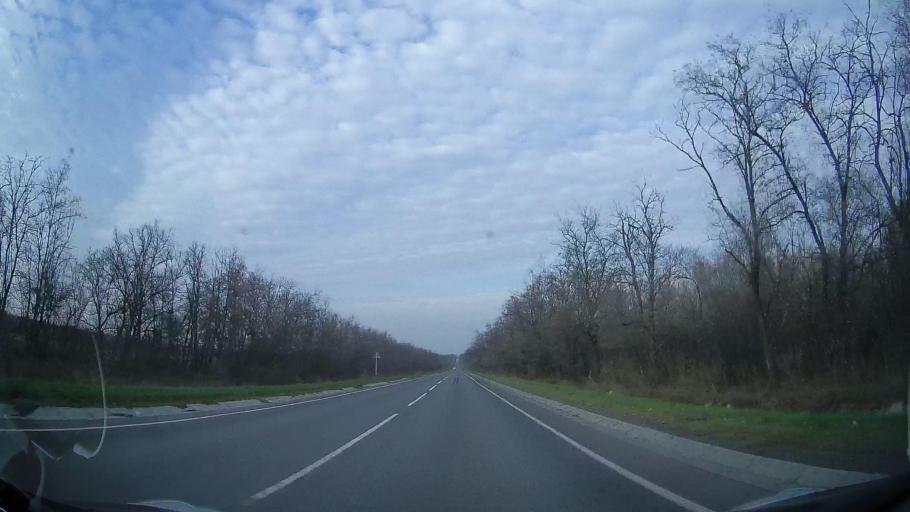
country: RU
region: Rostov
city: Bagayevskaya
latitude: 47.1047
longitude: 40.2767
